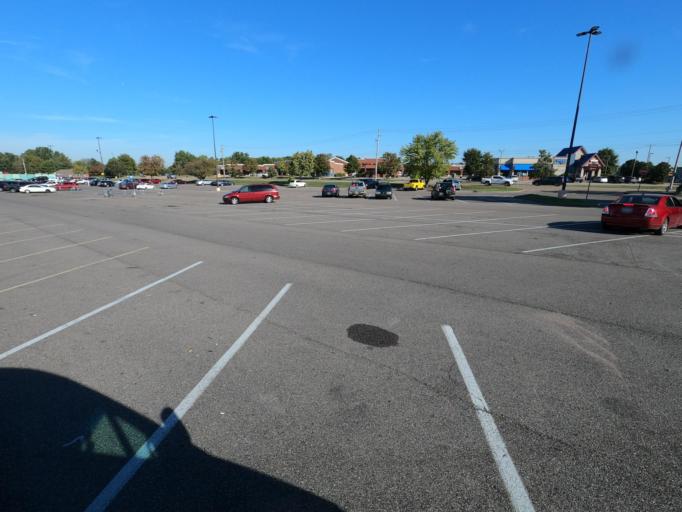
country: US
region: Tennessee
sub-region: Shelby County
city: Millington
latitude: 35.3573
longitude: -89.8956
